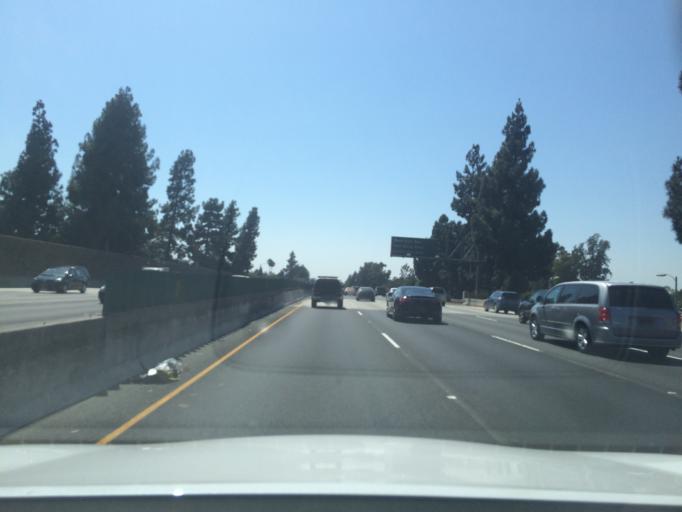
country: US
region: California
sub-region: Los Angeles County
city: Sherman Oaks
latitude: 34.1568
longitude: -118.4130
